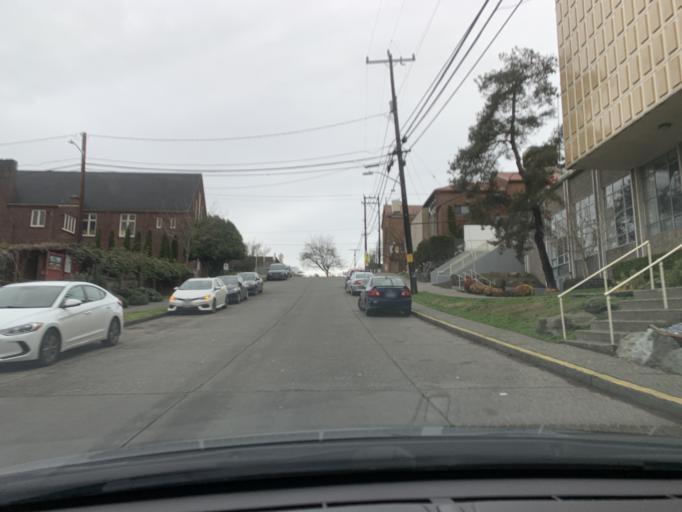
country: US
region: Washington
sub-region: King County
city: White Center
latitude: 47.5647
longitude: -122.3843
